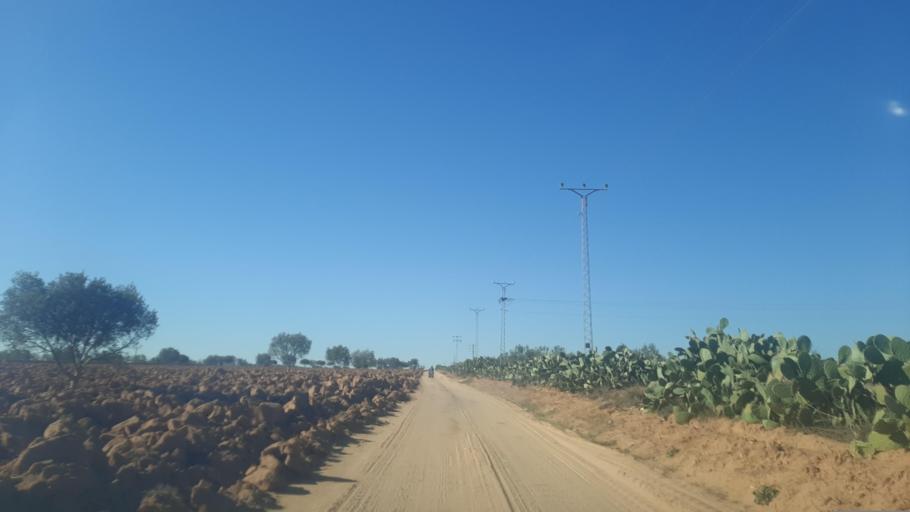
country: TN
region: Safaqis
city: Sfax
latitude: 34.8912
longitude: 10.5918
